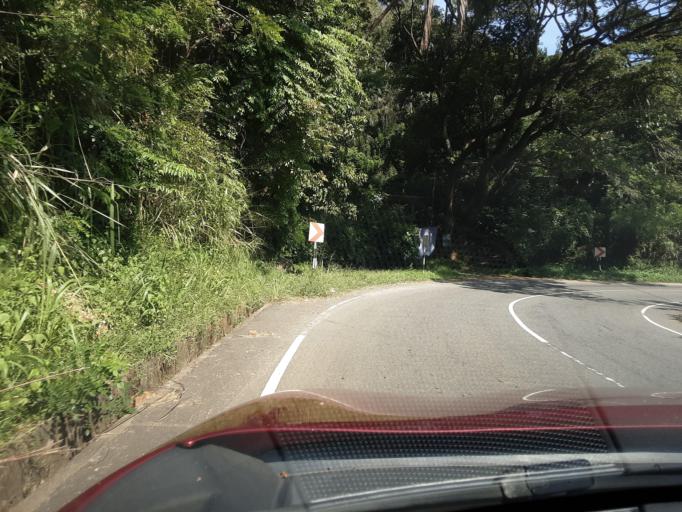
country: LK
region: Uva
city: Badulla
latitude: 7.0419
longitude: 81.0607
